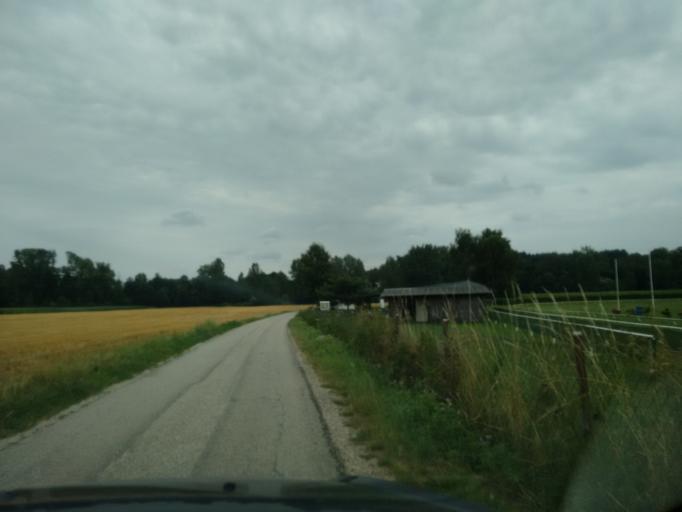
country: AT
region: Upper Austria
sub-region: Politischer Bezirk Grieskirchen
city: Bad Schallerbach
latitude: 48.2071
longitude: 13.9288
